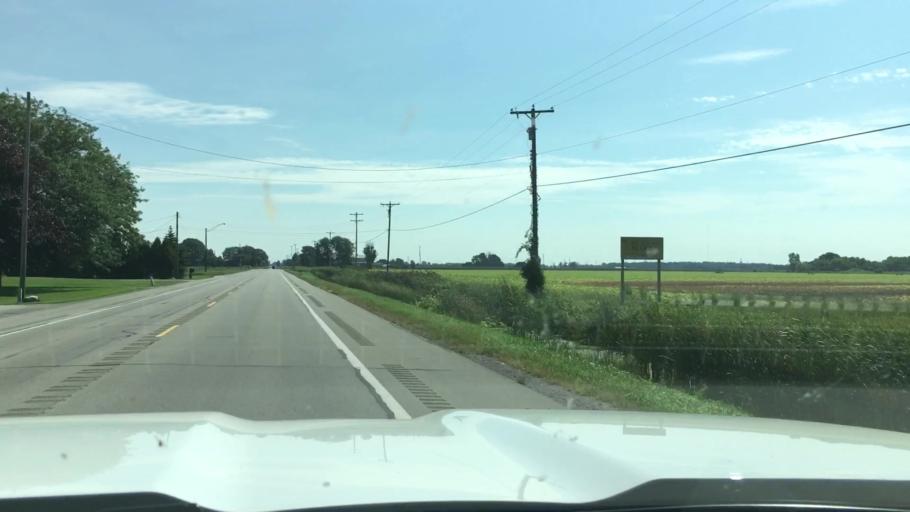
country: US
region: Michigan
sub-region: Bay County
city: Essexville
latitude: 43.5916
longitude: -83.7568
